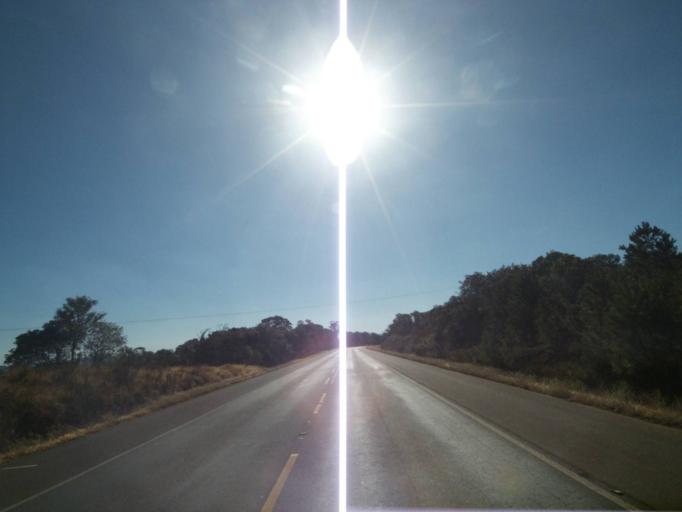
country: BR
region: Parana
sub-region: Tibagi
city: Tibagi
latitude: -24.6843
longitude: -50.4428
